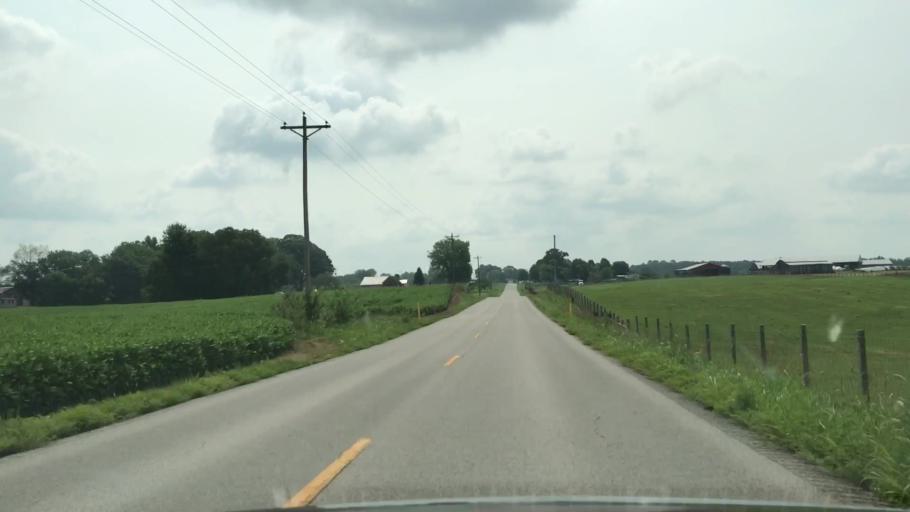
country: US
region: Kentucky
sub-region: Edmonson County
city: Brownsville
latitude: 37.1387
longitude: -86.1791
